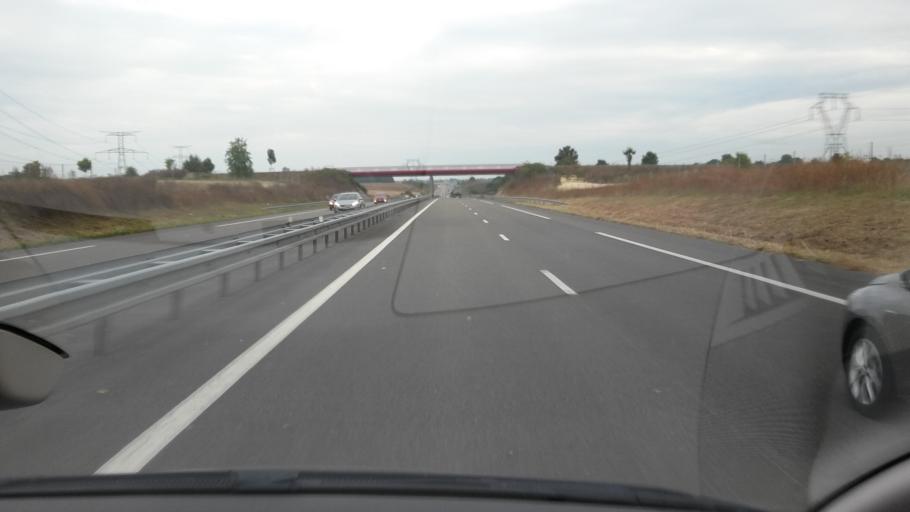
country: FR
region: Champagne-Ardenne
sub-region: Departement des Ardennes
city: Rethel
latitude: 49.5650
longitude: 4.4688
